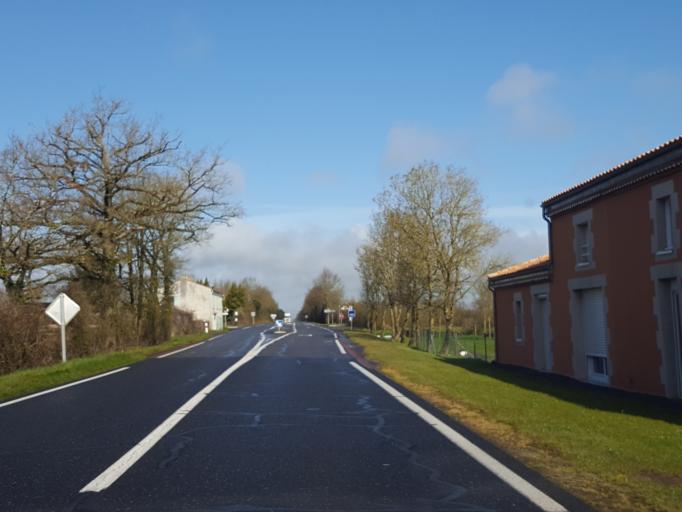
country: FR
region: Pays de la Loire
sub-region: Departement de la Vendee
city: Saligny
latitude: 46.8051
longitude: -1.4537
